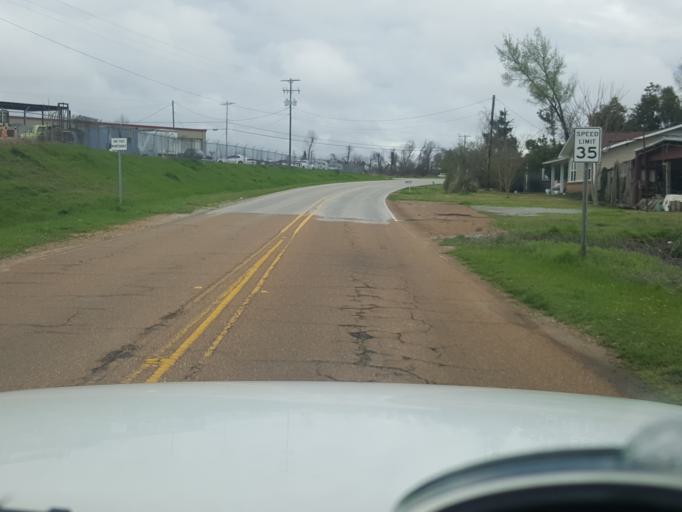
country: US
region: Mississippi
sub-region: Yazoo County
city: Yazoo City
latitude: 32.8406
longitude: -90.3830
